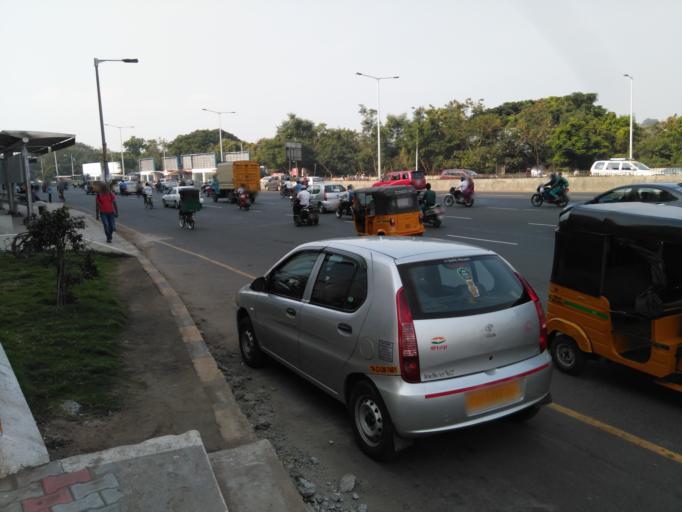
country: IN
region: Tamil Nadu
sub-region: Kancheepuram
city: Alandur
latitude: 13.0050
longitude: 80.2018
